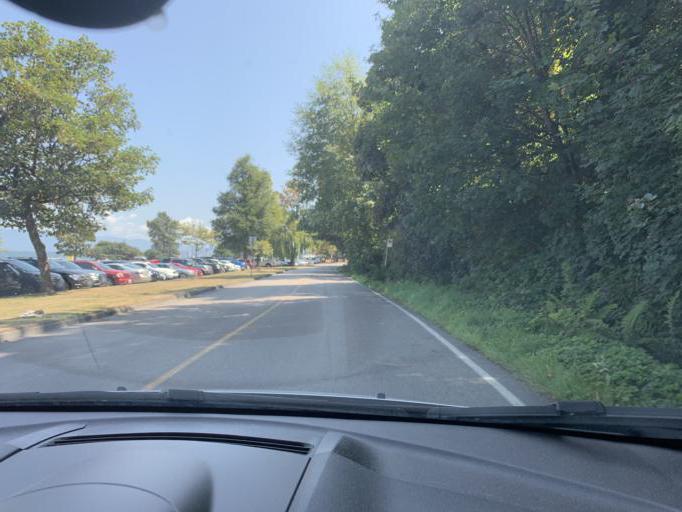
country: CA
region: British Columbia
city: West End
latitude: 49.2764
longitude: -123.2187
